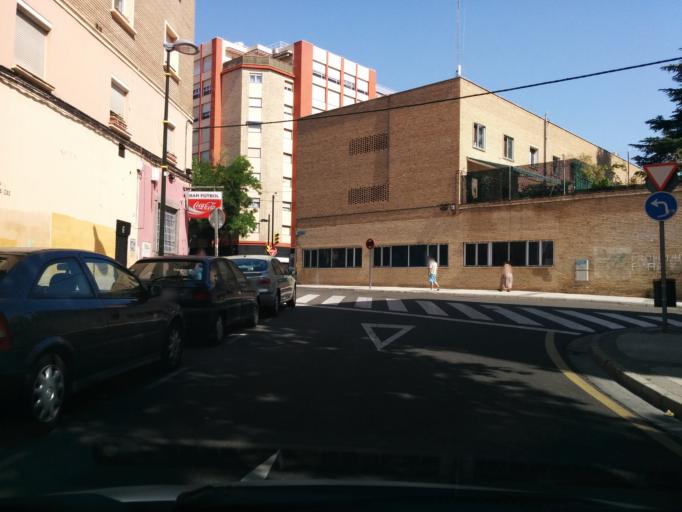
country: ES
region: Aragon
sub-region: Provincia de Zaragoza
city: Zaragoza
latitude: 41.6321
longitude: -0.8847
